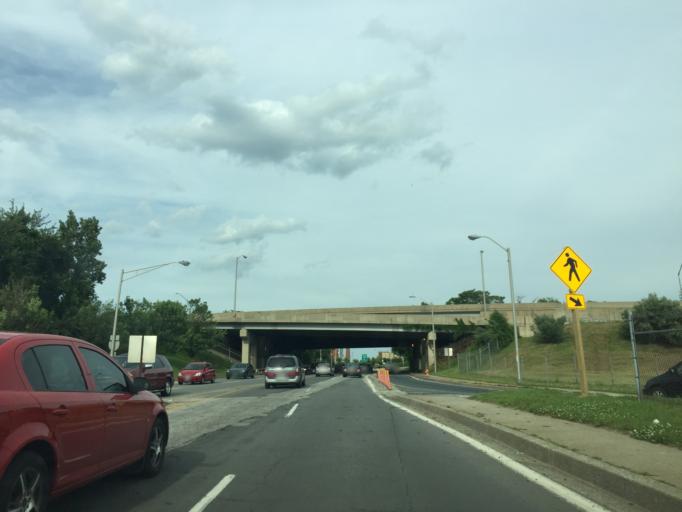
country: US
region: Maryland
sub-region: Baltimore County
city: Rosedale
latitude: 39.2918
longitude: -76.5549
